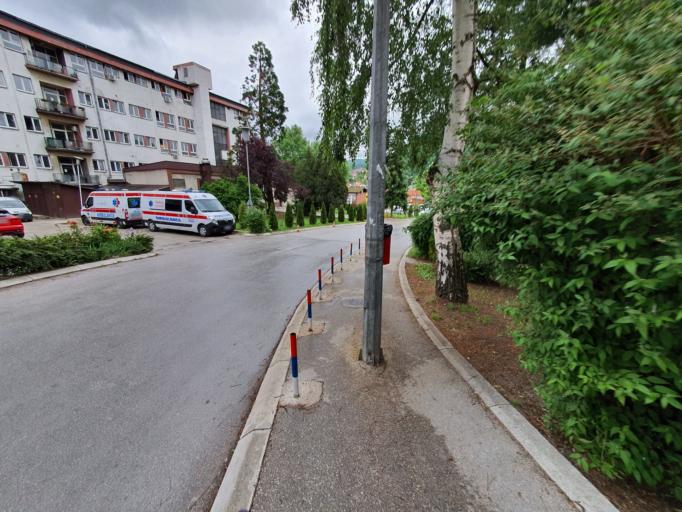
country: RS
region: Central Serbia
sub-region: Zlatiborski Okrug
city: Uzice
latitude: 43.8516
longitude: 19.8592
